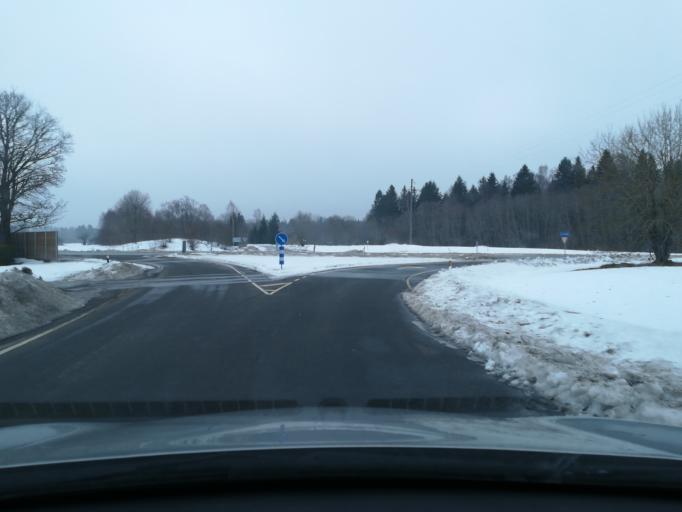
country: EE
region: Harju
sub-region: Loksa linn
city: Loksa
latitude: 59.4643
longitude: 25.7045
